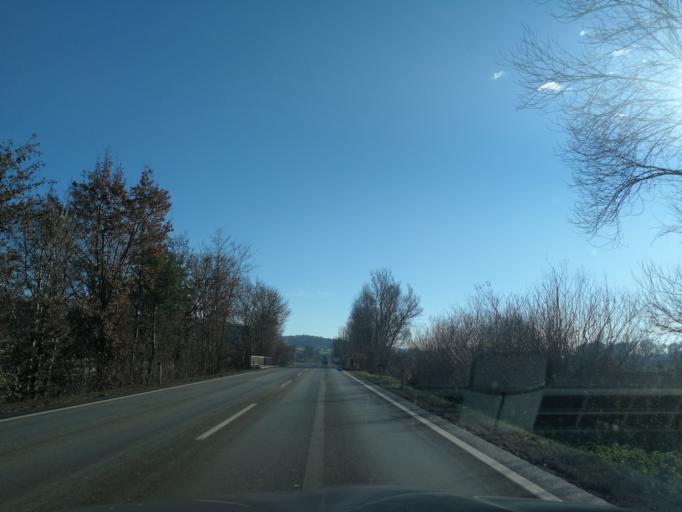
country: AT
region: Styria
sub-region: Politischer Bezirk Weiz
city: Hofstatten an der Raab
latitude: 47.0753
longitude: 15.7443
